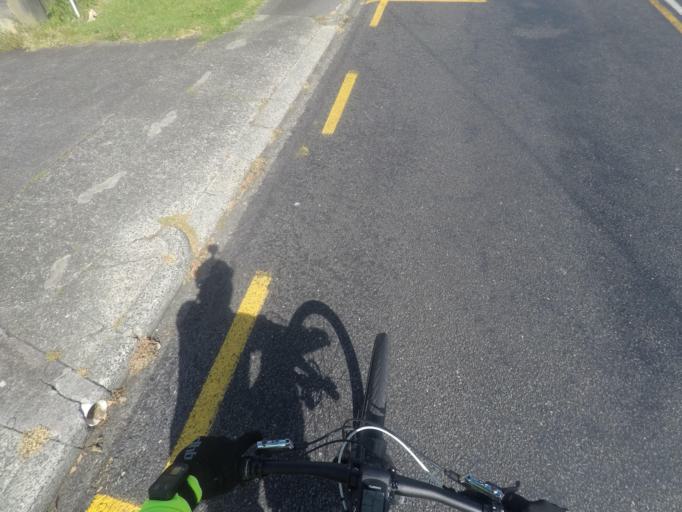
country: NZ
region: Auckland
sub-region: Auckland
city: Auckland
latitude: -36.9234
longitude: 174.7632
